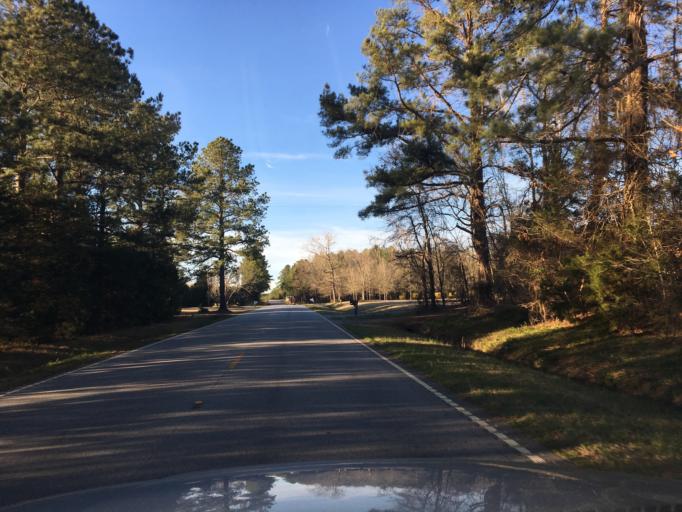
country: US
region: South Carolina
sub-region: Saluda County
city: Saluda
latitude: 34.0676
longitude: -81.8179
